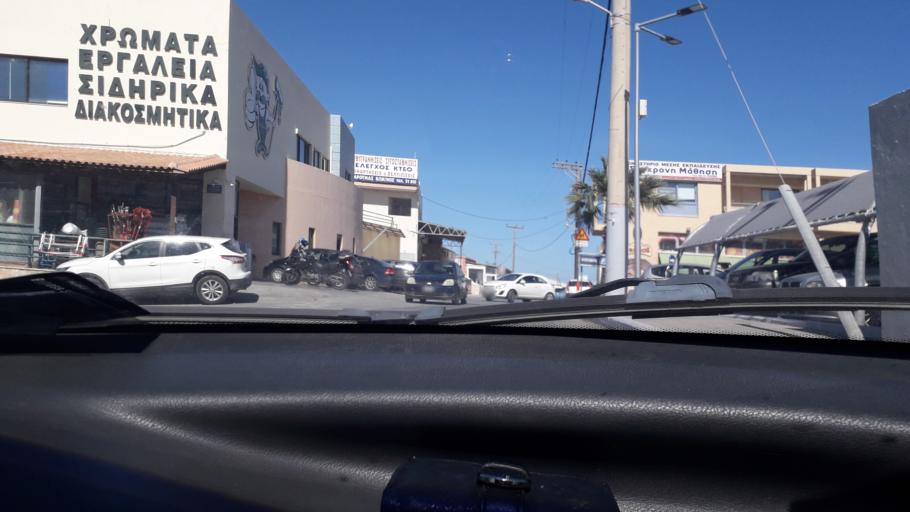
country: GR
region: Crete
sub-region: Nomos Rethymnis
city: Atsipopoulon
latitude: 35.3628
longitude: 24.4446
